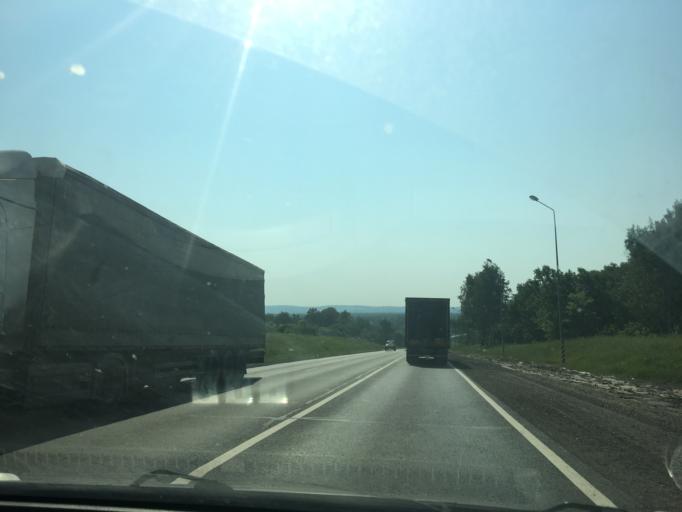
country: RU
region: Nizjnij Novgorod
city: Kstovo
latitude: 56.1025
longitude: 44.2985
